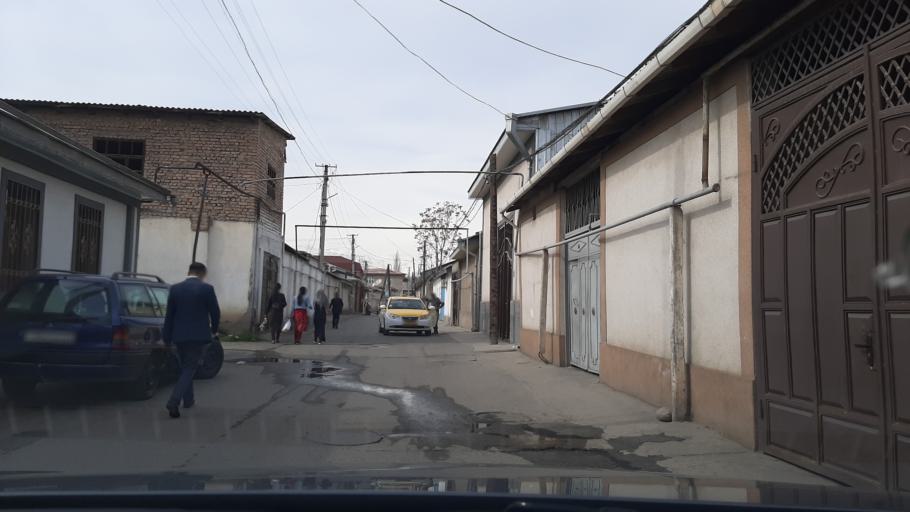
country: TJ
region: Dushanbe
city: Dushanbe
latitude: 38.5629
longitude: 68.7748
